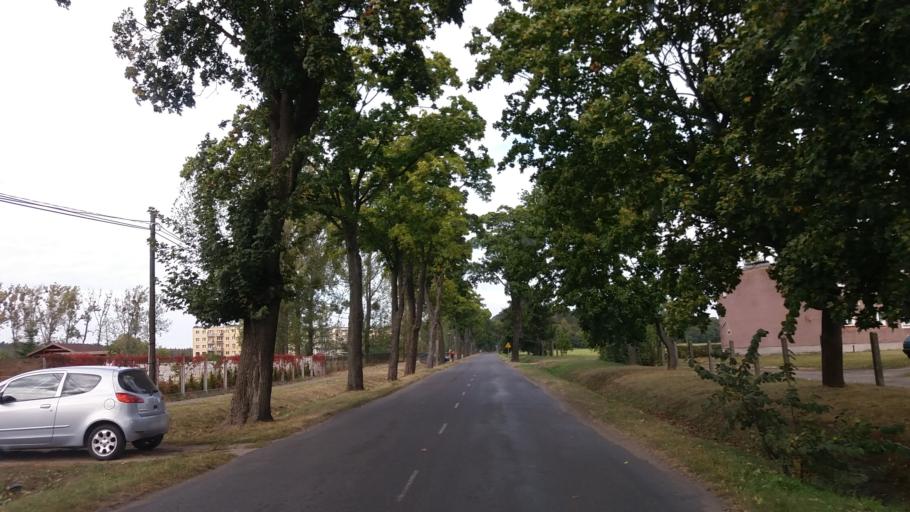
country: PL
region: Lubusz
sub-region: Powiat strzelecko-drezdenecki
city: Strzelce Krajenskie
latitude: 52.9561
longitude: 15.4531
